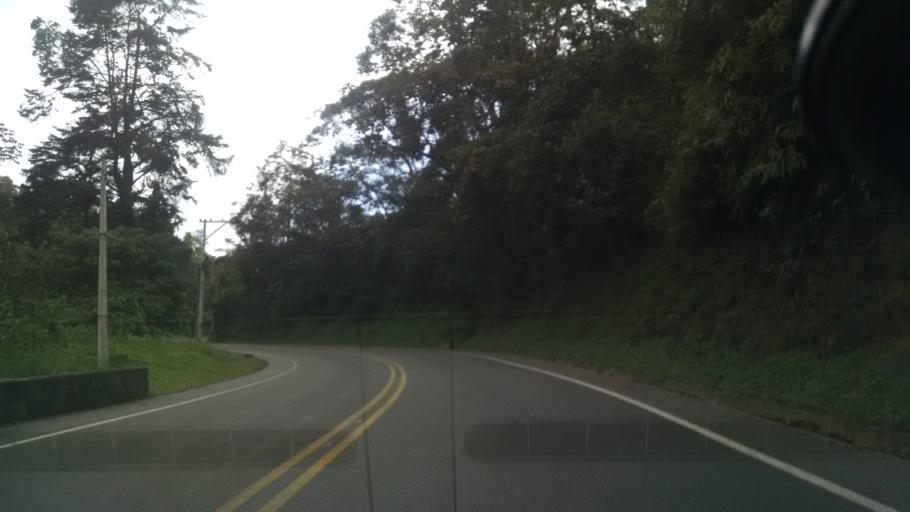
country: CO
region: Antioquia
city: Caldas
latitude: 6.0486
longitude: -75.6292
